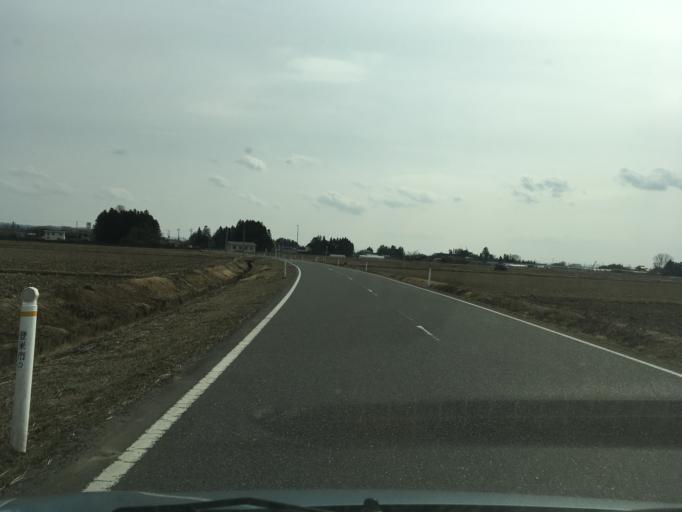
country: JP
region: Miyagi
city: Wakuya
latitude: 38.7241
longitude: 141.2400
